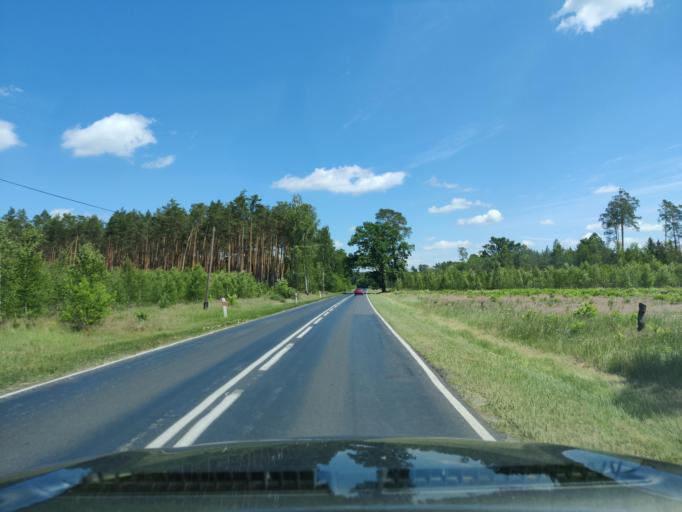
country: PL
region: Greater Poland Voivodeship
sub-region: Powiat nowotomyski
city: Nowy Tomysl
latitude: 52.2296
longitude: 16.1095
